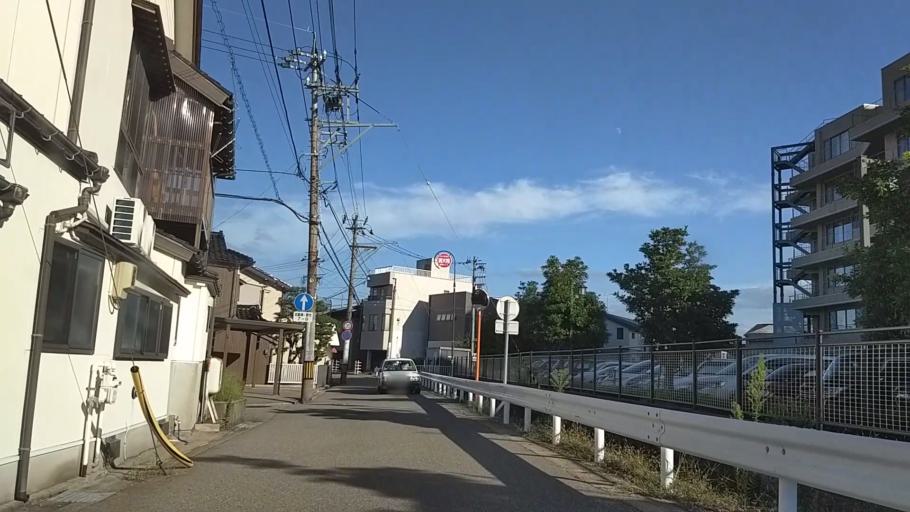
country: JP
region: Ishikawa
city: Kanazawa-shi
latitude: 36.5742
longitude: 136.6422
